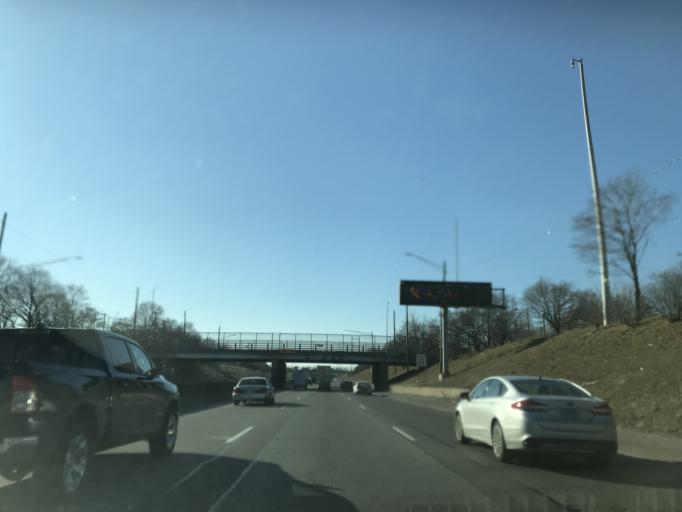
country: US
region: Michigan
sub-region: Wayne County
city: Hamtramck
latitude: 42.3893
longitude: -83.0130
